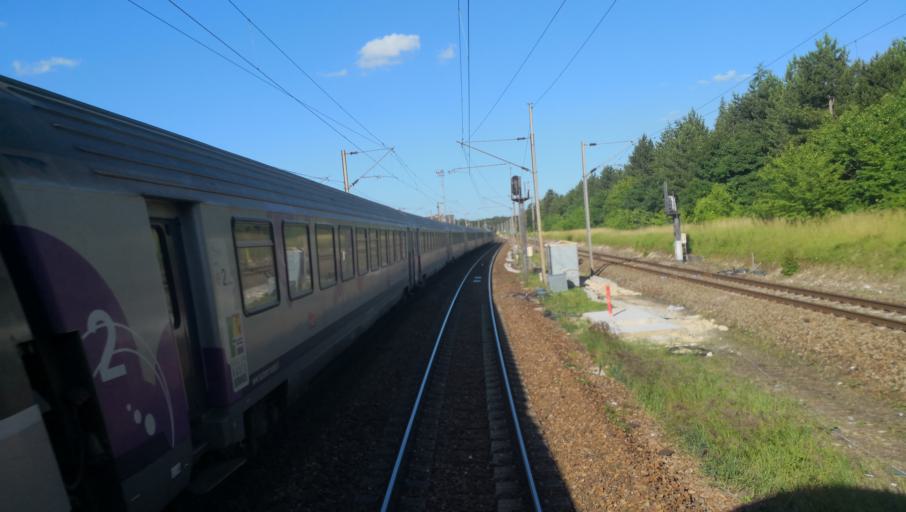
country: FR
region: Ile-de-France
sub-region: Departement des Yvelines
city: Le Mesnil-le-Roi
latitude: 48.9577
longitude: 2.1027
